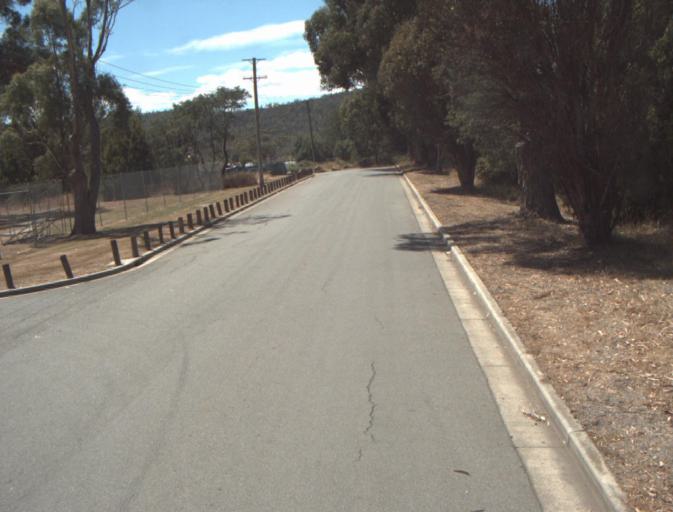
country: AU
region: Tasmania
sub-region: Launceston
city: Mayfield
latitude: -41.3742
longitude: 147.1318
